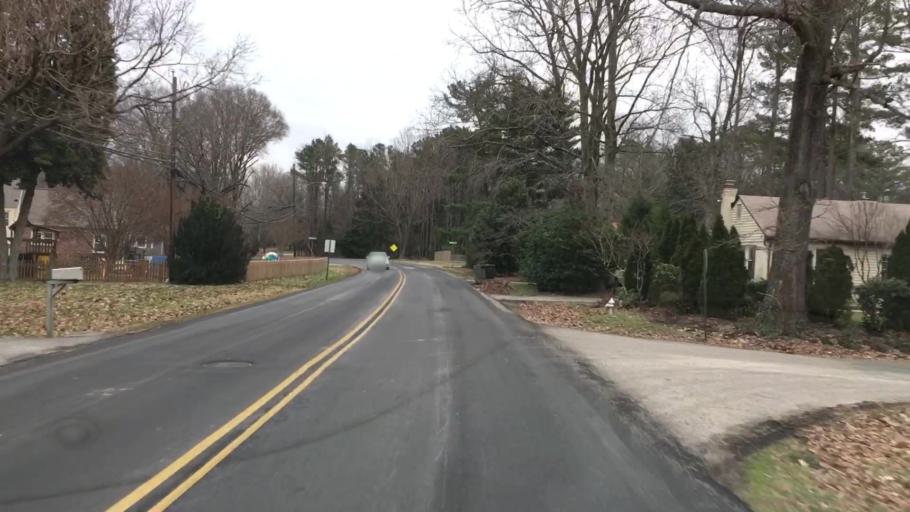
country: US
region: Virginia
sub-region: Chesterfield County
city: Bon Air
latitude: 37.5406
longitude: -77.5710
